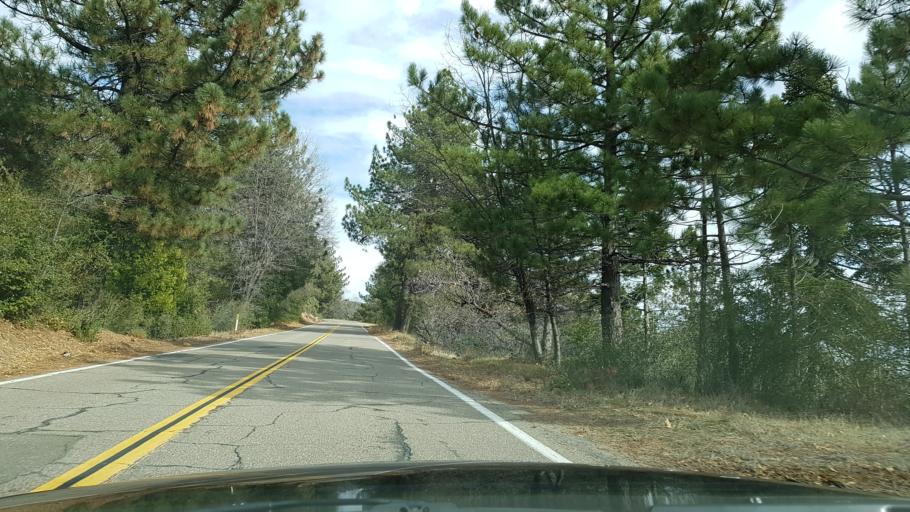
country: US
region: California
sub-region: Riverside County
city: Aguanga
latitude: 33.3445
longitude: -116.8735
